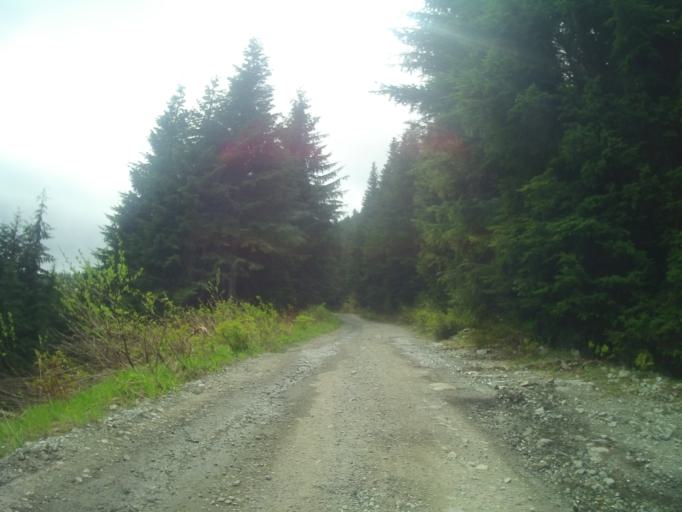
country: CA
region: British Columbia
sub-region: Fraser Valley Regional District
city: North Vancouver
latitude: 49.3855
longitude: -123.0681
